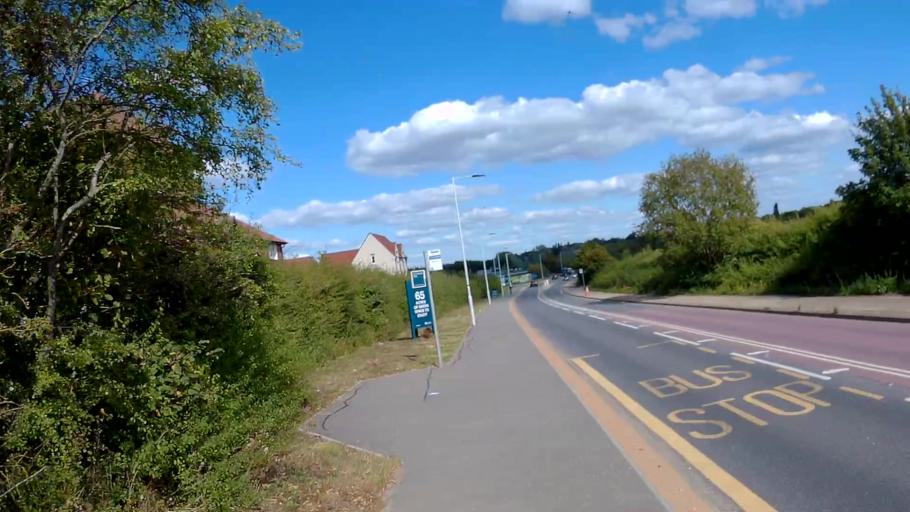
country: GB
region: England
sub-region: Bracknell Forest
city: Bracknell
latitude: 51.4284
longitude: -0.7599
